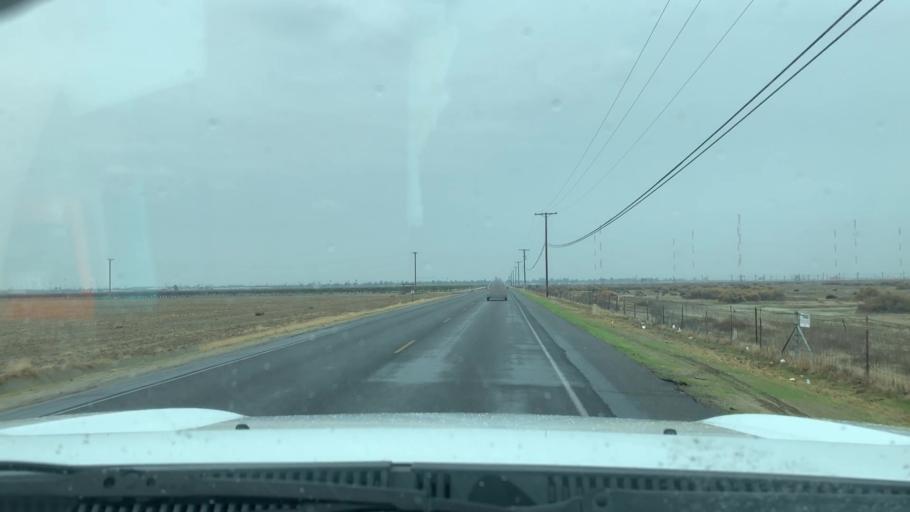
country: US
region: California
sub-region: Kern County
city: Delano
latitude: 35.7613
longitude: -119.2875
